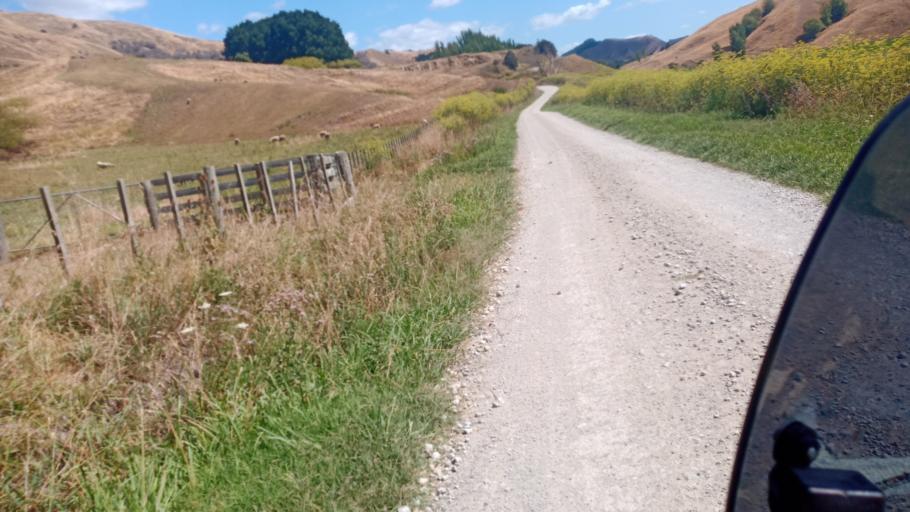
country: NZ
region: Gisborne
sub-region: Gisborne District
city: Gisborne
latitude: -38.5132
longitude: 177.7326
